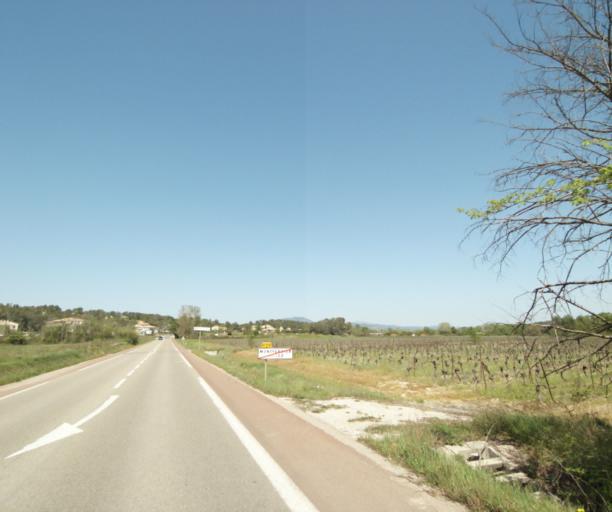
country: FR
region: Languedoc-Roussillon
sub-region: Departement de l'Herault
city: Montferrier-sur-Lez
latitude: 43.6748
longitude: 3.8584
